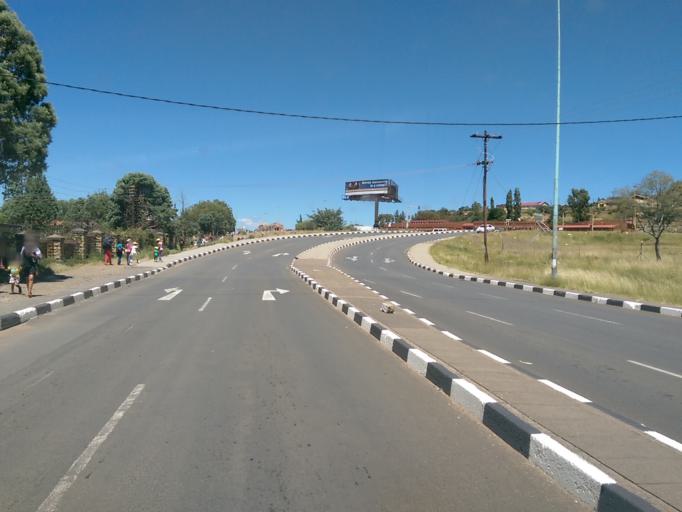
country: LS
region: Maseru
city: Maseru
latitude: -29.3241
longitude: 27.5001
